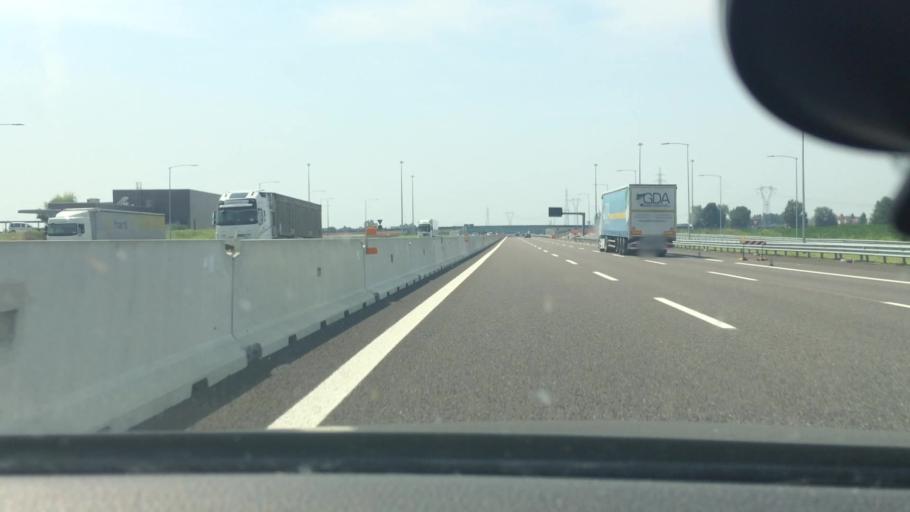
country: IT
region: Lombardy
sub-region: Provincia di Lodi
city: Merlino
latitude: 45.4284
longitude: 9.4221
